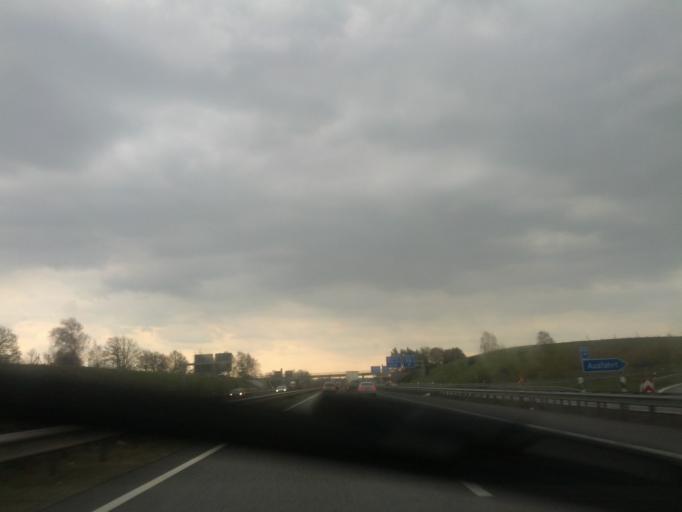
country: DE
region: Lower Saxony
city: Langwedel
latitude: 53.0023
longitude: 9.1737
